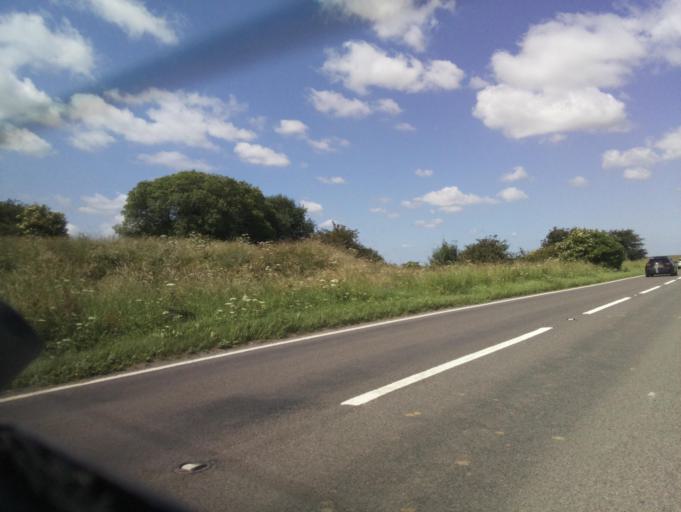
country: GB
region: England
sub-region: Derbyshire
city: Bakewell
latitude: 53.1635
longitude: -1.7753
